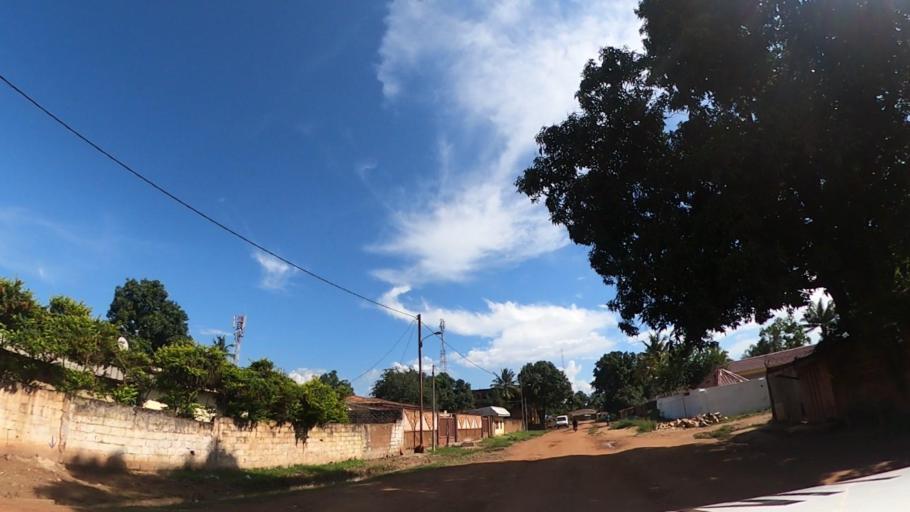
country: CF
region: Bangui
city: Bangui
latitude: 4.3756
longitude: 18.5505
